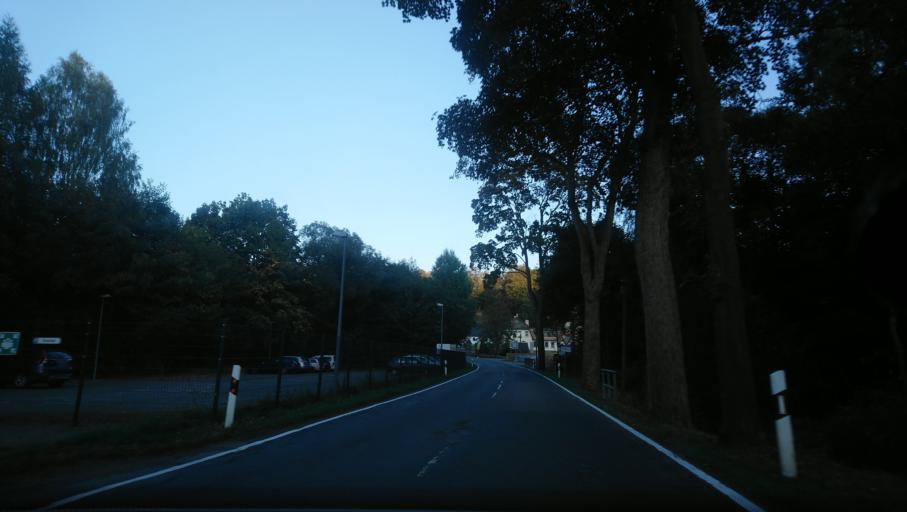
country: DE
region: Saxony
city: Wiesa
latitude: 50.6041
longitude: 12.9924
